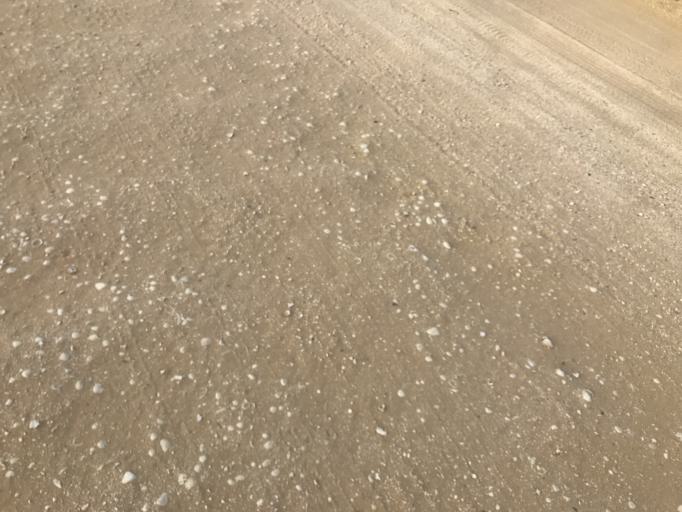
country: SN
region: Saint-Louis
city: Saint-Louis
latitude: 16.0296
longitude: -16.4450
